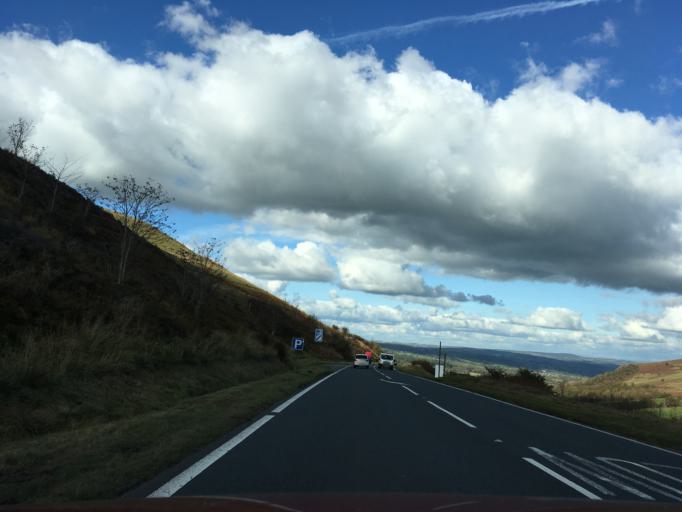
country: GB
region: Wales
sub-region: Sir Powys
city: Cray
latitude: 51.8793
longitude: -3.4948
